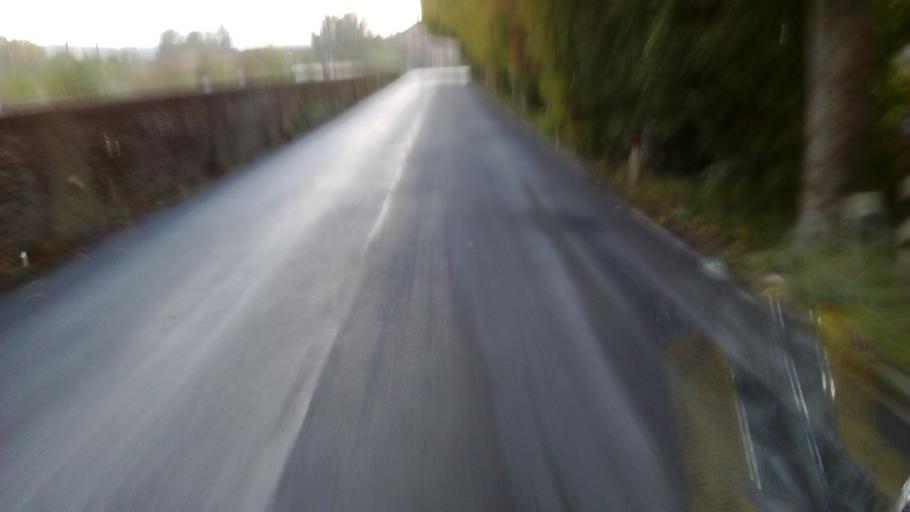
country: IT
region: Tuscany
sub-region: Province of Florence
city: Castelfiorentino
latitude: 43.6489
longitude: 10.9502
